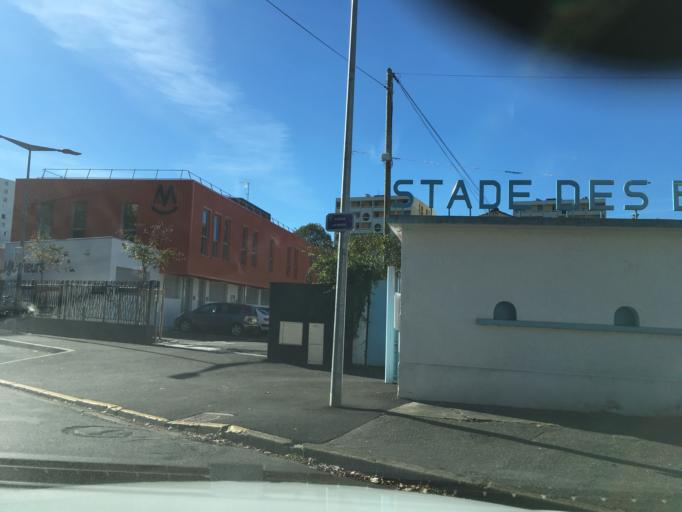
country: FR
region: Aquitaine
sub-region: Departement des Pyrenees-Atlantiques
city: Pau
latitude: 43.3090
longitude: -0.3526
